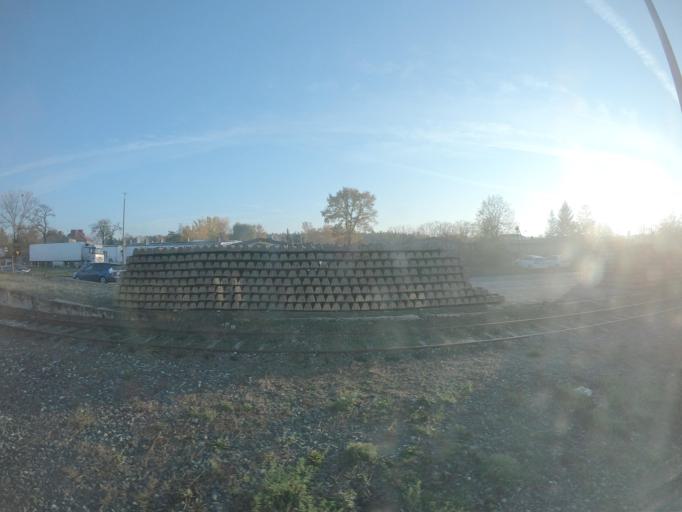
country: PL
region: Lubusz
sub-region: Powiat slubicki
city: Rzepin
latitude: 52.3497
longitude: 14.8179
